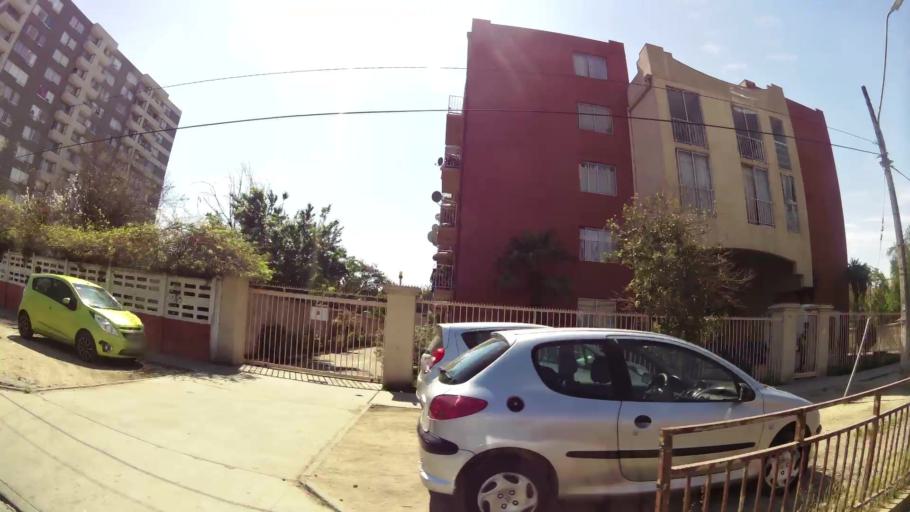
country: CL
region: Santiago Metropolitan
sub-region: Provincia de Santiago
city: La Pintana
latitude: -33.5412
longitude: -70.6599
